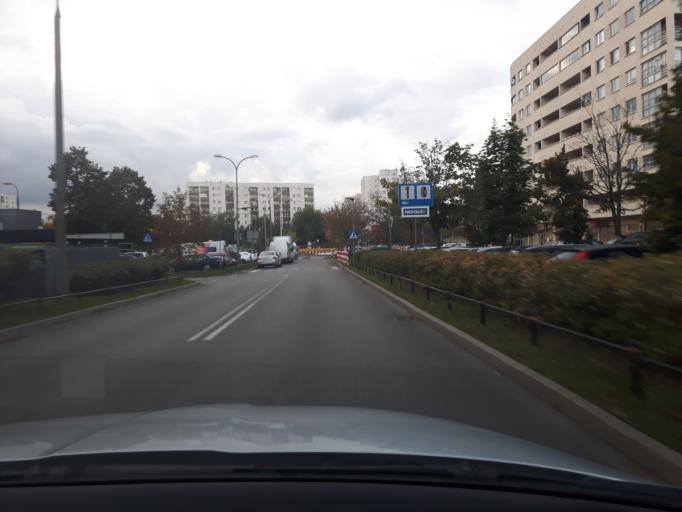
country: PL
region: Masovian Voivodeship
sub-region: Warszawa
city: Ursynow
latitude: 52.1425
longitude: 21.0502
